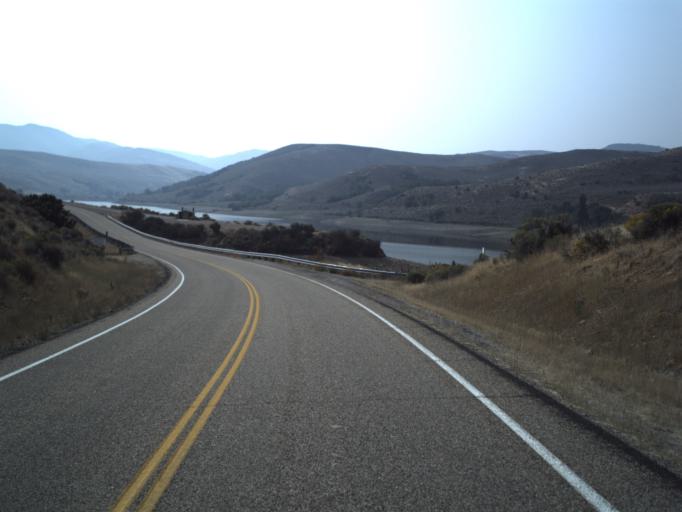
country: US
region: Utah
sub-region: Summit County
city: Summit Park
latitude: 40.8999
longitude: -111.5885
